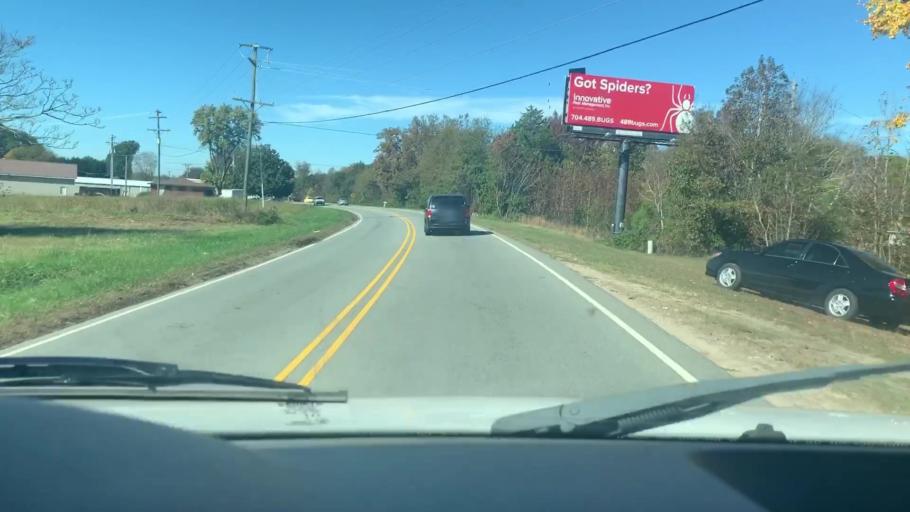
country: US
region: North Carolina
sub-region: Lincoln County
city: Lowesville
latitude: 35.4411
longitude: -80.9815
